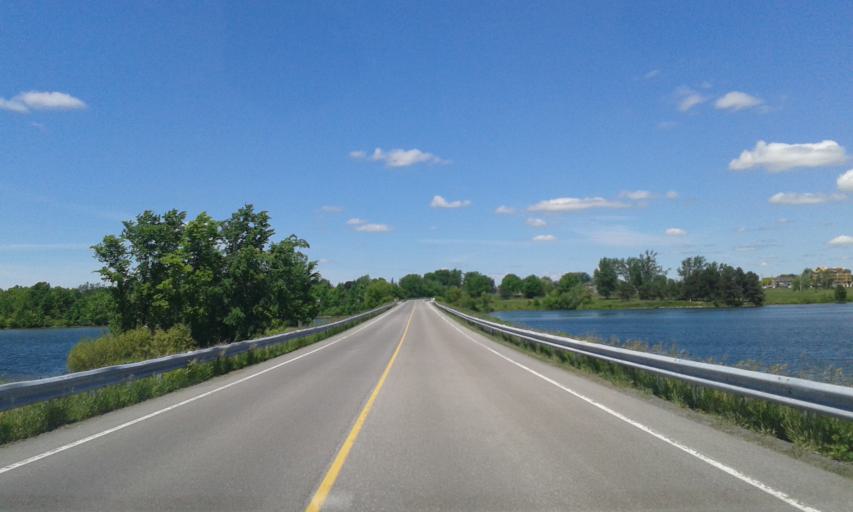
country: US
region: New York
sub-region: St. Lawrence County
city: Massena
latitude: 45.0212
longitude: -74.8938
